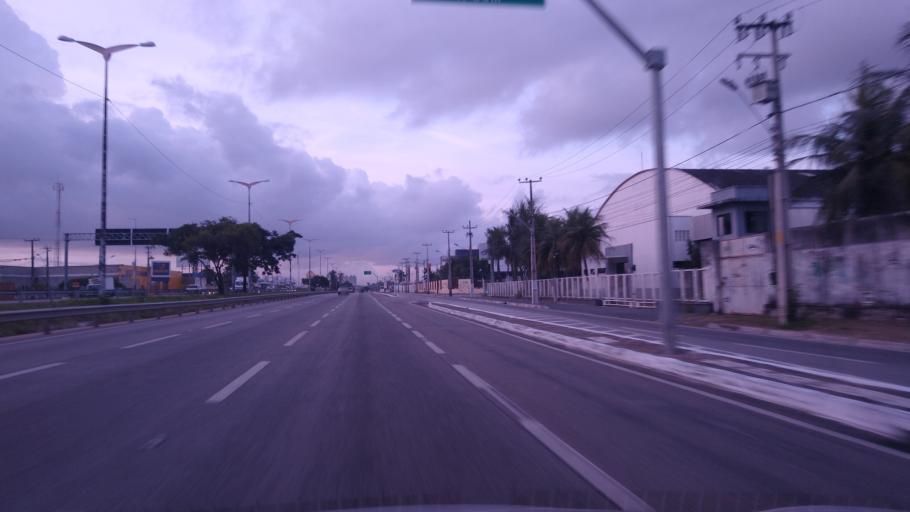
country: BR
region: Ceara
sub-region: Fortaleza
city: Fortaleza
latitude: -3.7863
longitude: -38.5117
